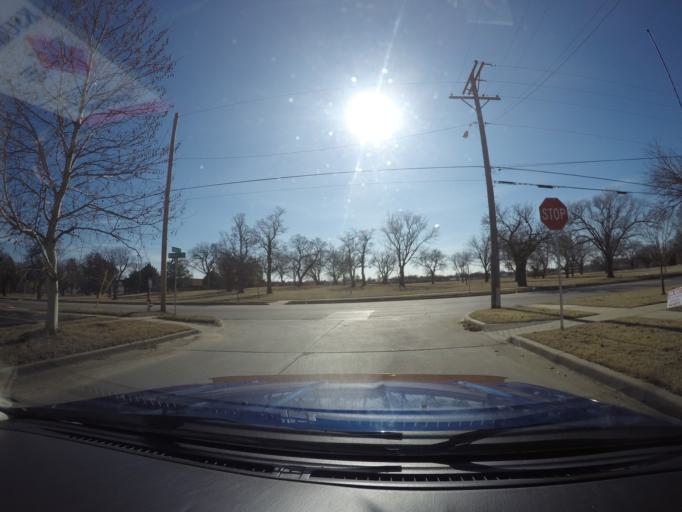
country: US
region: Kansas
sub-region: Sedgwick County
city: Wichita
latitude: 37.6841
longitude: -97.3827
